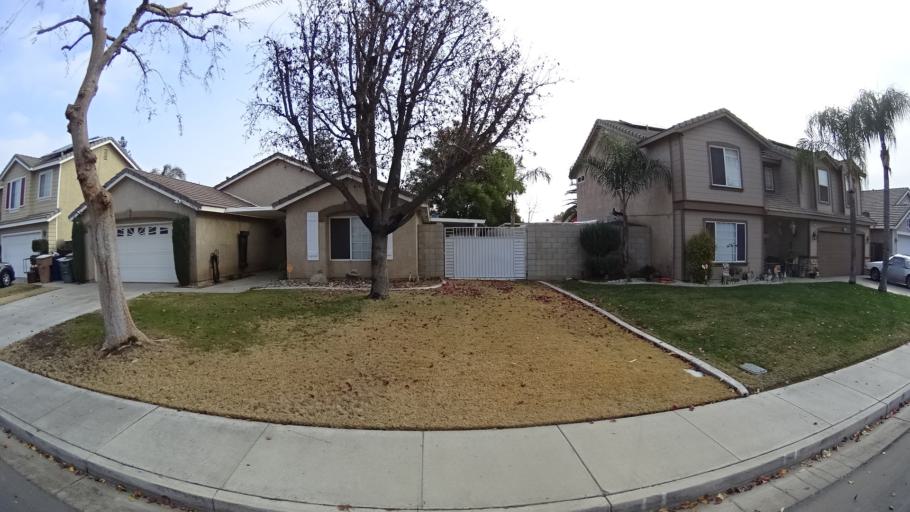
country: US
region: California
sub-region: Kern County
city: Greenfield
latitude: 35.3018
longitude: -119.0681
